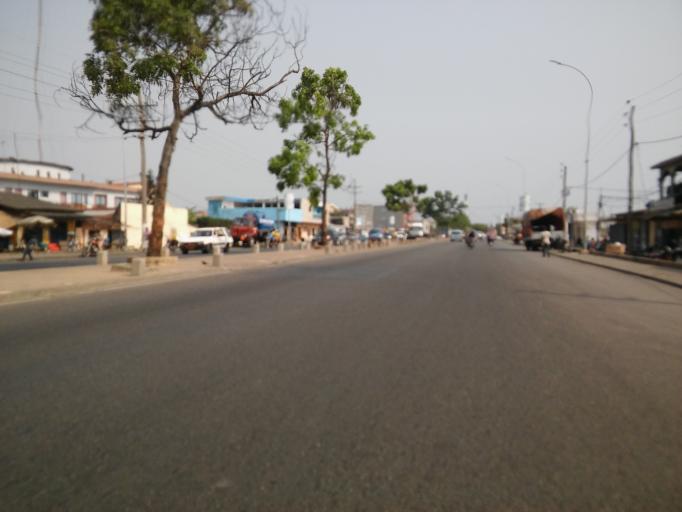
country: BJ
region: Littoral
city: Cotonou
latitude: 6.3739
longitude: 2.4069
